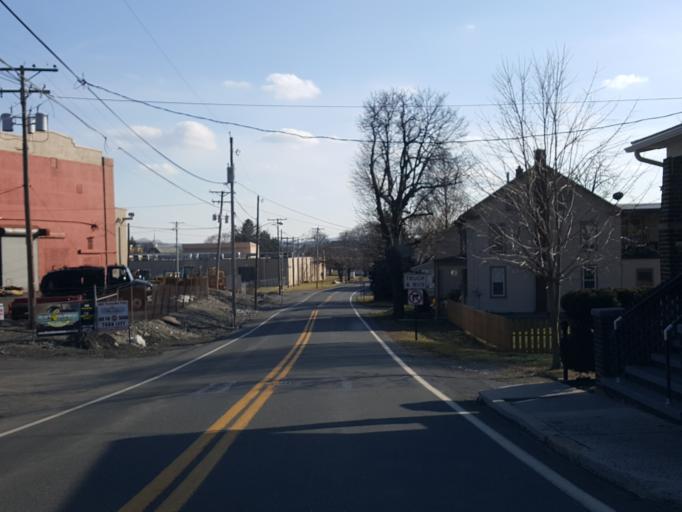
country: US
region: Pennsylvania
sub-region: Lebanon County
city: Pleasant Hill
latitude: 40.3484
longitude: -76.4498
